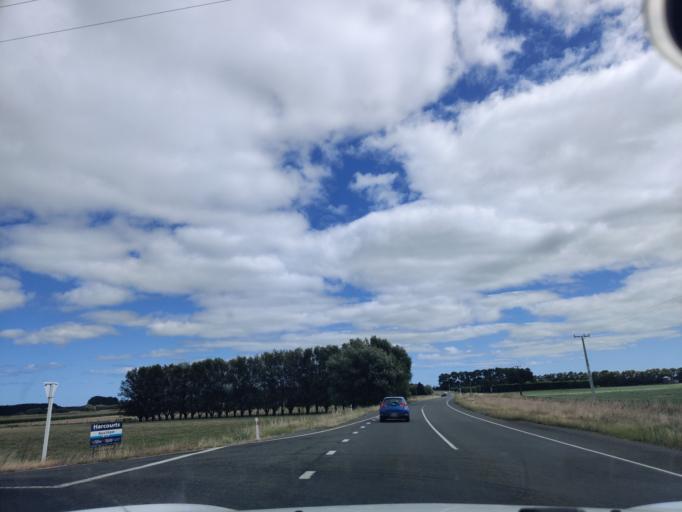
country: NZ
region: Manawatu-Wanganui
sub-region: Horowhenua District
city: Foxton
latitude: -40.4251
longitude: 175.4535
